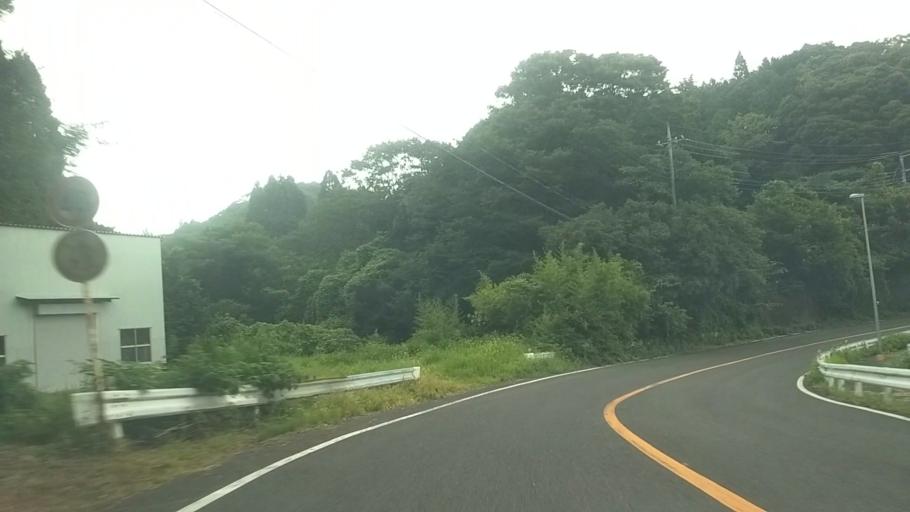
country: JP
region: Chiba
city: Katsuura
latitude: 35.2468
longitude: 140.1937
